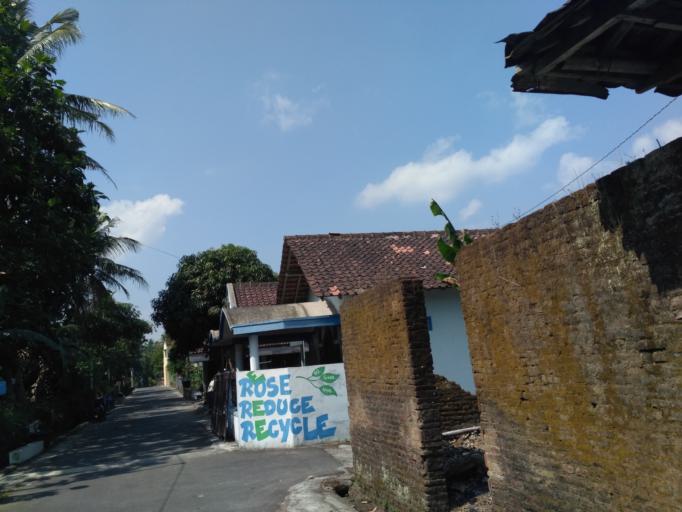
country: ID
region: Daerah Istimewa Yogyakarta
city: Melati
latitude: -7.7074
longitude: 110.4164
